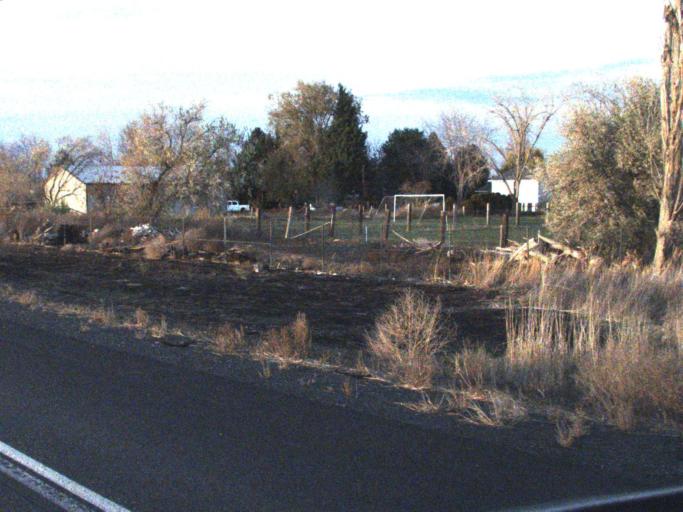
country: US
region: Washington
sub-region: Walla Walla County
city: Burbank
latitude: 46.1926
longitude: -118.9888
